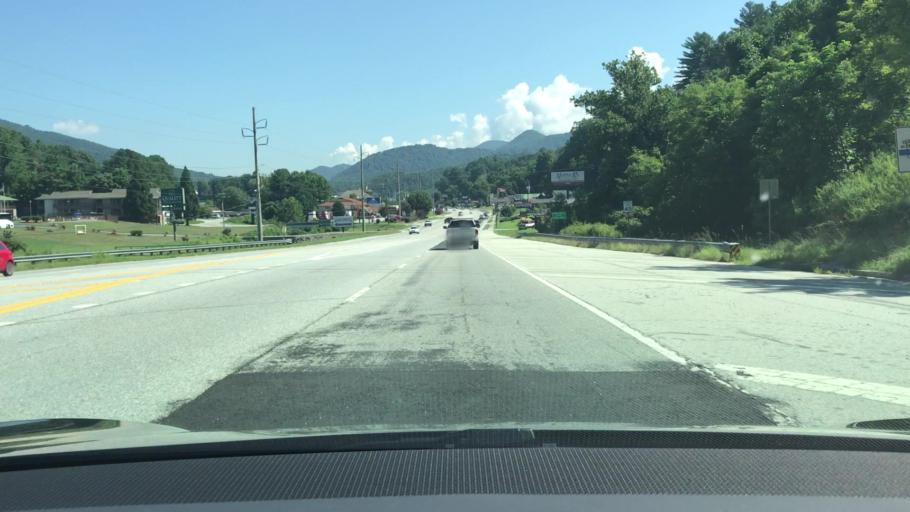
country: US
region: Georgia
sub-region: Rabun County
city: Clayton
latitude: 34.8652
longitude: -83.4035
